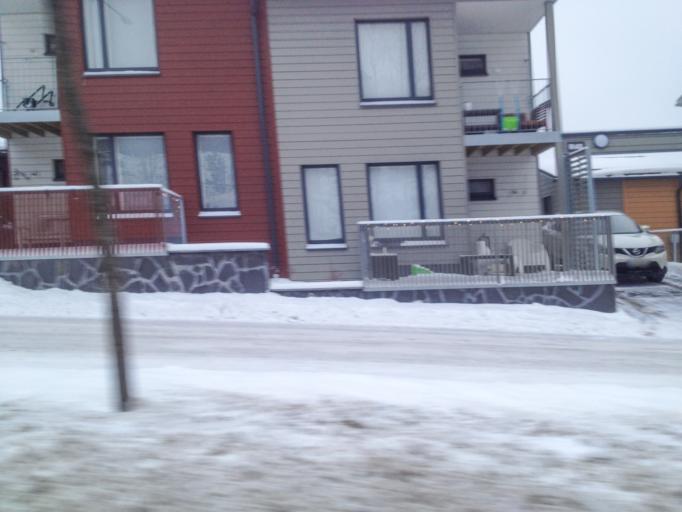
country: FI
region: Uusimaa
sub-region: Helsinki
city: Vantaa
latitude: 60.2166
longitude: 25.0613
